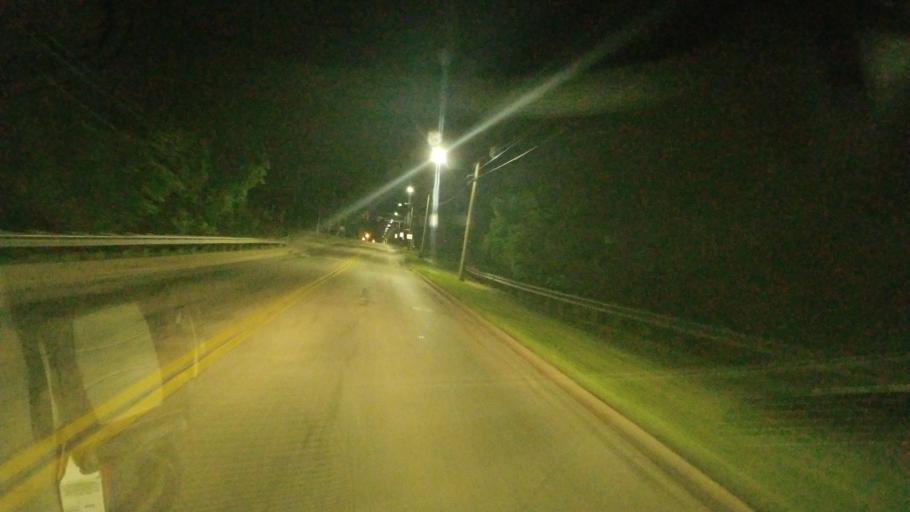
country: US
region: Ohio
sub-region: Trumbull County
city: McKinley Heights
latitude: 41.1822
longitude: -80.7319
